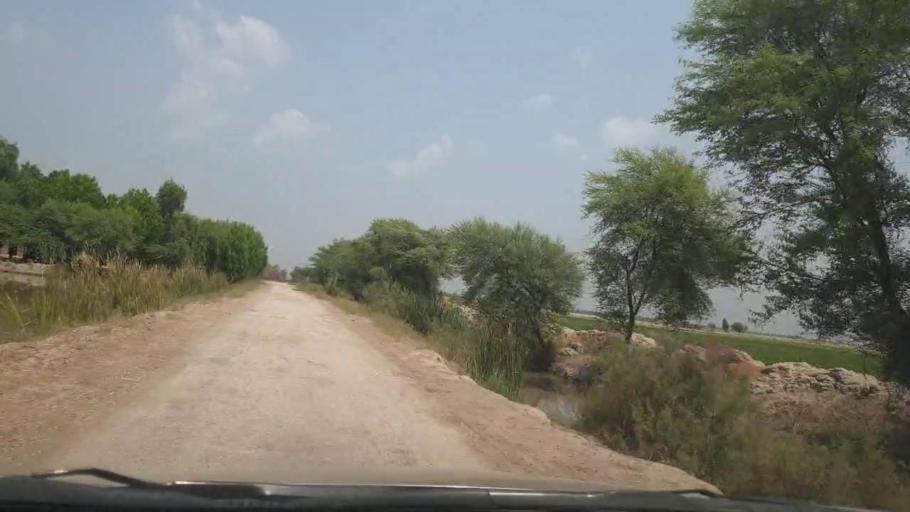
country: PK
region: Sindh
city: Ratodero
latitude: 27.6967
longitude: 68.2330
